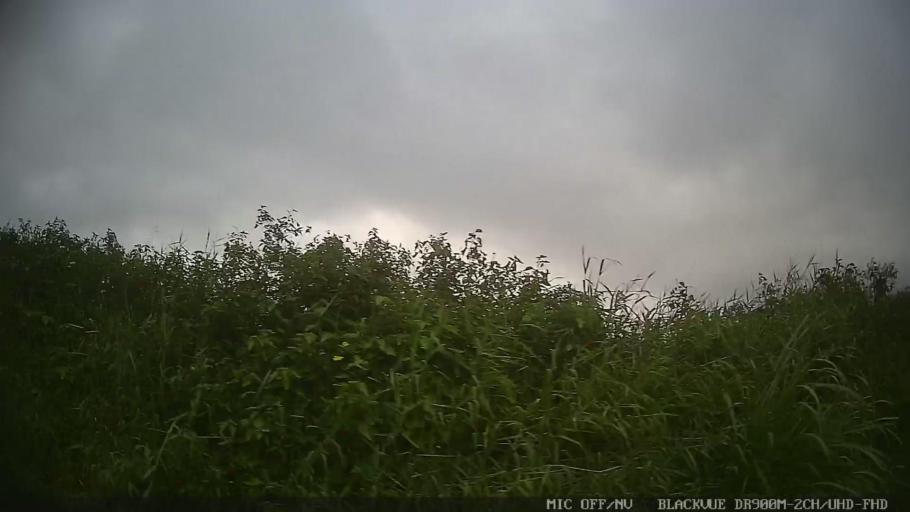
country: BR
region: Sao Paulo
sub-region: Biritiba-Mirim
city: Biritiba Mirim
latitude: -23.5504
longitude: -46.0860
